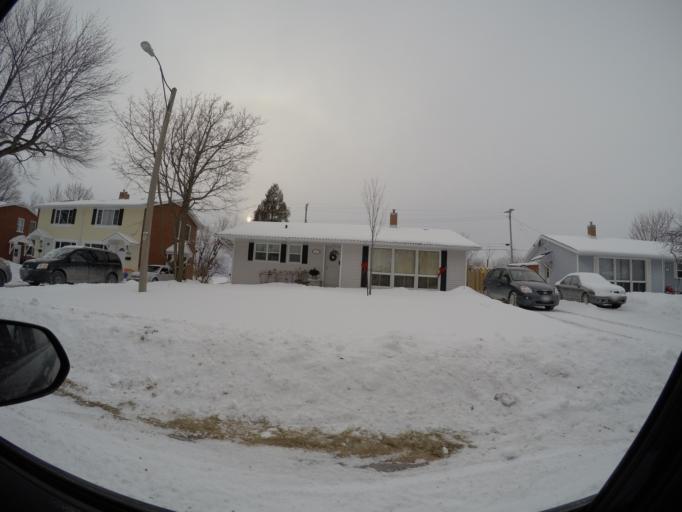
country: CA
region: Ontario
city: Kingston
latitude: 44.2375
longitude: -76.4606
